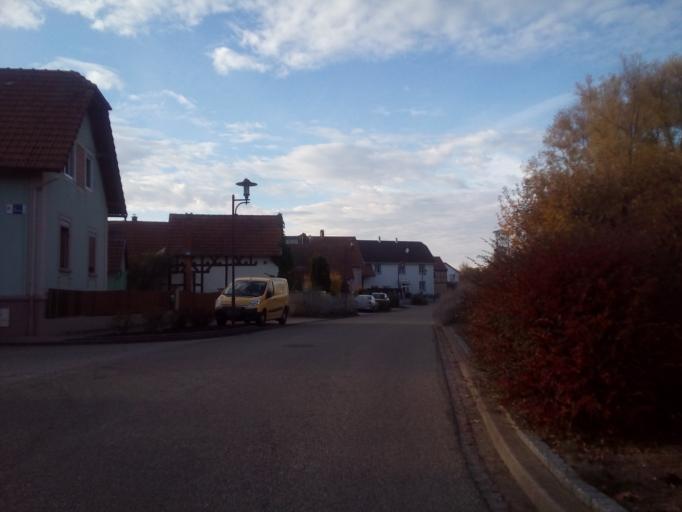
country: FR
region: Alsace
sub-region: Departement du Bas-Rhin
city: Herrlisheim
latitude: 48.7096
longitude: 7.9161
